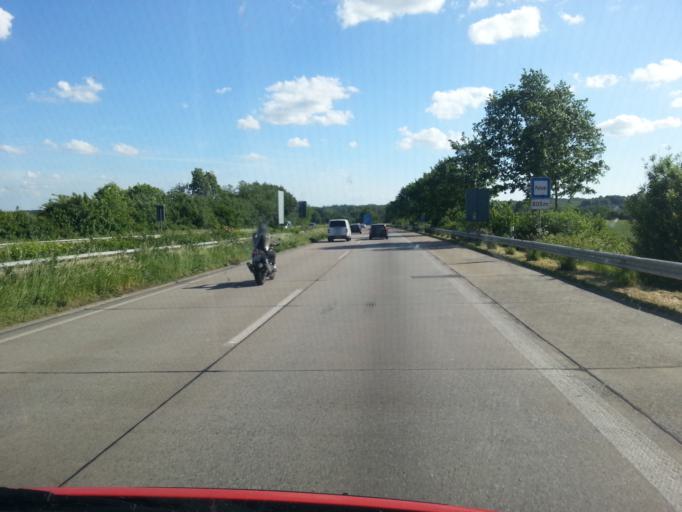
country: DE
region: Schleswig-Holstein
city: Susel
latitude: 54.0473
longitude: 10.7299
